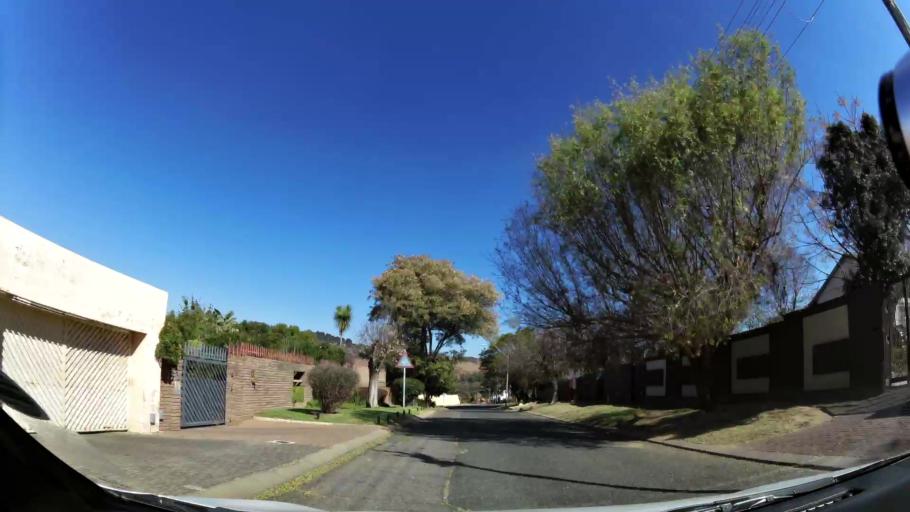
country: ZA
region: Gauteng
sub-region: City of Johannesburg Metropolitan Municipality
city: Johannesburg
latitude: -26.2751
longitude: 27.9927
